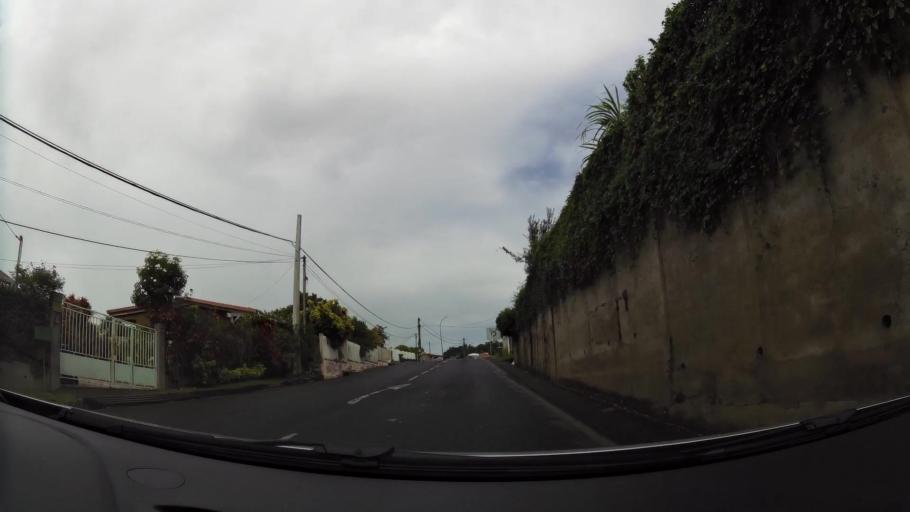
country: MQ
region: Martinique
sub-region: Martinique
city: Le Lamentin
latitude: 14.6255
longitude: -61.0184
